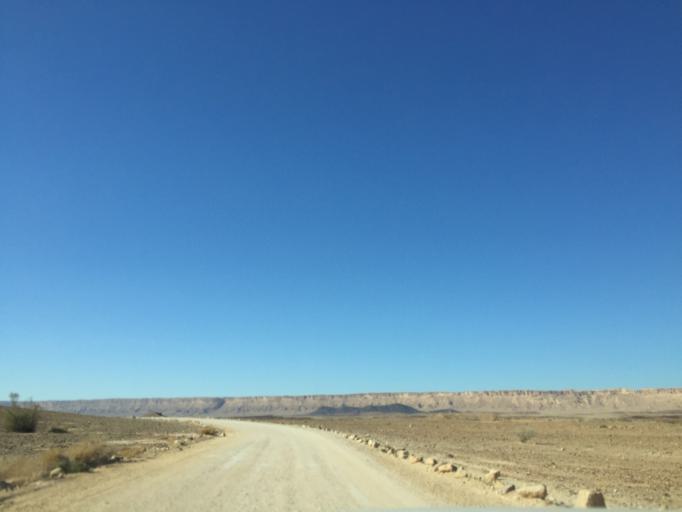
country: IL
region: Southern District
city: Mitzpe Ramon
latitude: 30.6239
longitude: 34.9255
